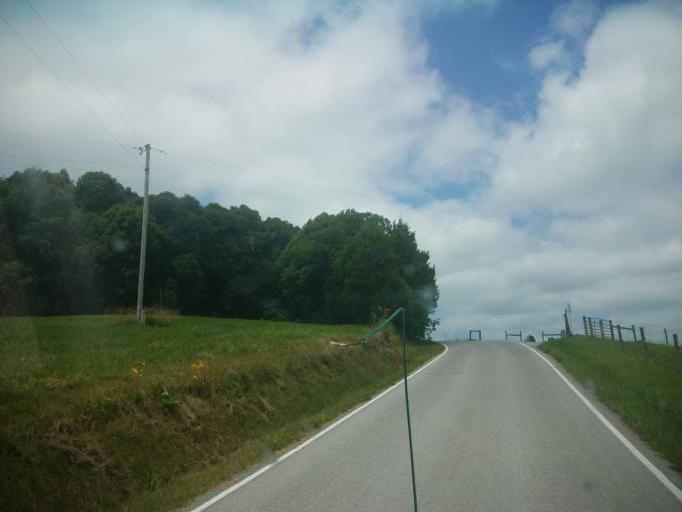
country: US
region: Kentucky
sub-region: Hart County
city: Munfordville
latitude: 37.3399
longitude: -86.0354
